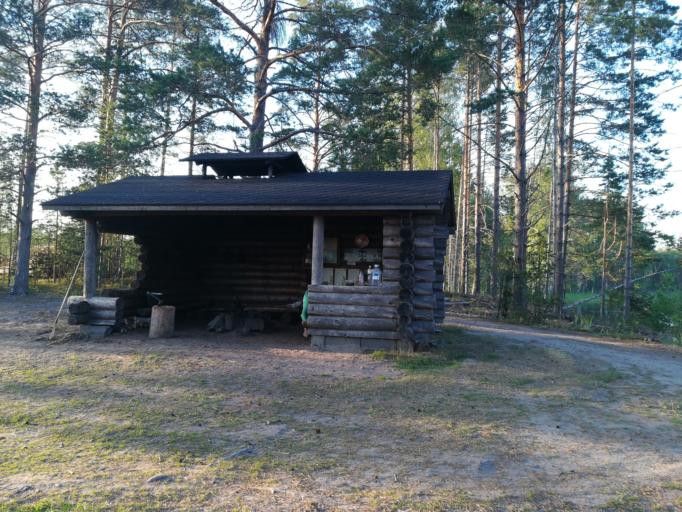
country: FI
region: Southern Savonia
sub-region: Mikkeli
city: Puumala
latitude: 61.4277
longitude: 28.4564
